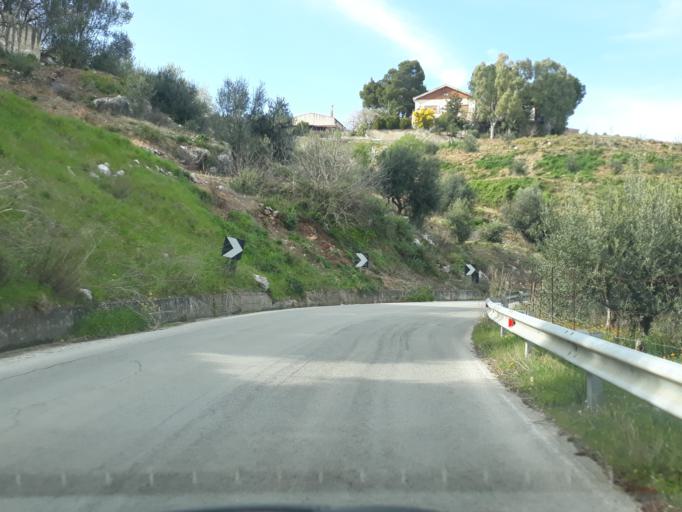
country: IT
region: Sicily
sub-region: Palermo
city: Altofonte
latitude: 38.0414
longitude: 13.3093
